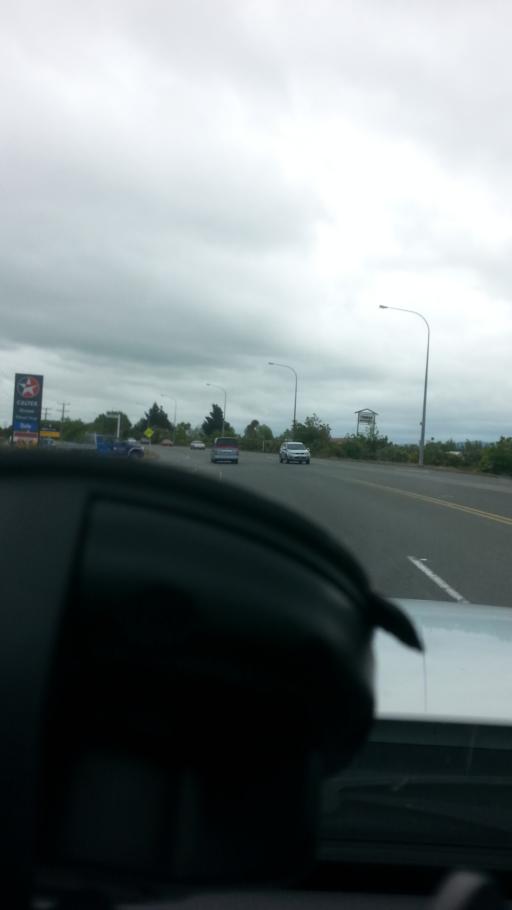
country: NZ
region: Wellington
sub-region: Masterton District
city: Masterton
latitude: -40.9626
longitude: 175.6130
